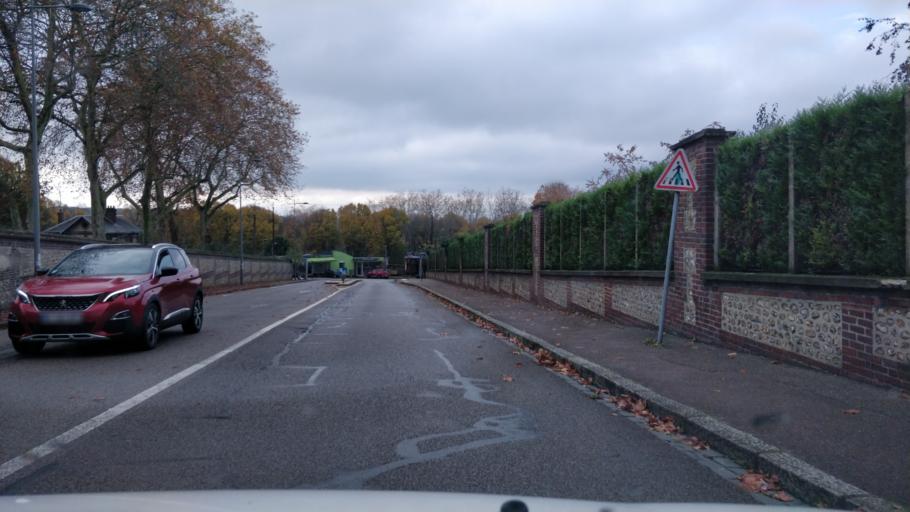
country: FR
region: Haute-Normandie
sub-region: Departement de la Seine-Maritime
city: Bihorel
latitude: 49.4500
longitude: 1.1209
